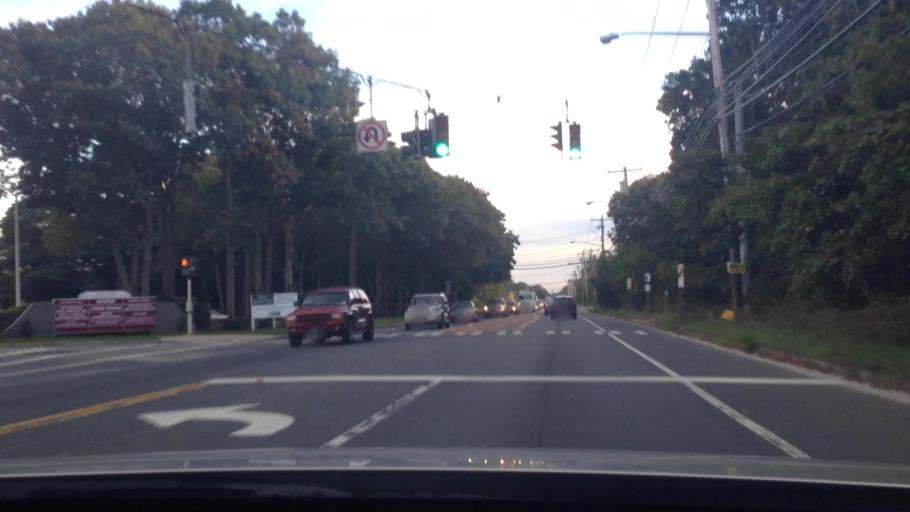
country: US
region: New York
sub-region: Suffolk County
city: Medford
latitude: 40.8427
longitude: -72.9968
